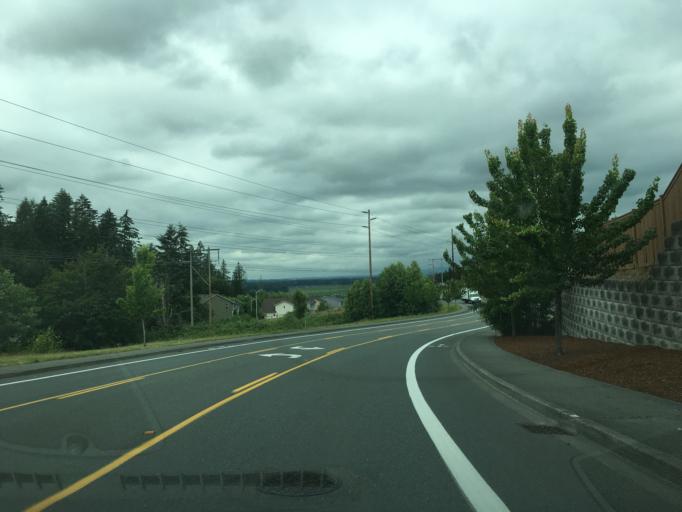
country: US
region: Washington
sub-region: Snohomish County
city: Sisco Heights
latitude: 48.0726
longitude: -122.1223
